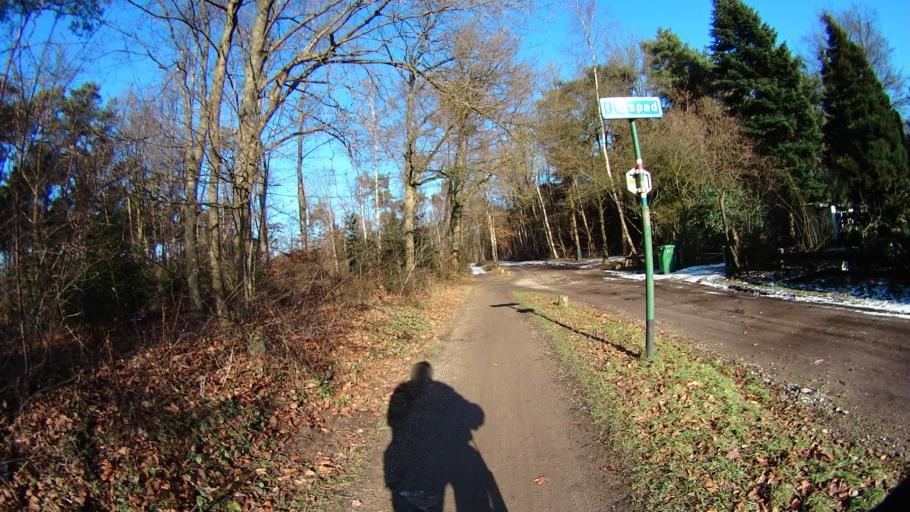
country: NL
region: North Holland
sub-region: Gemeente Laren
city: Laren
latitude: 52.2164
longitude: 5.2208
